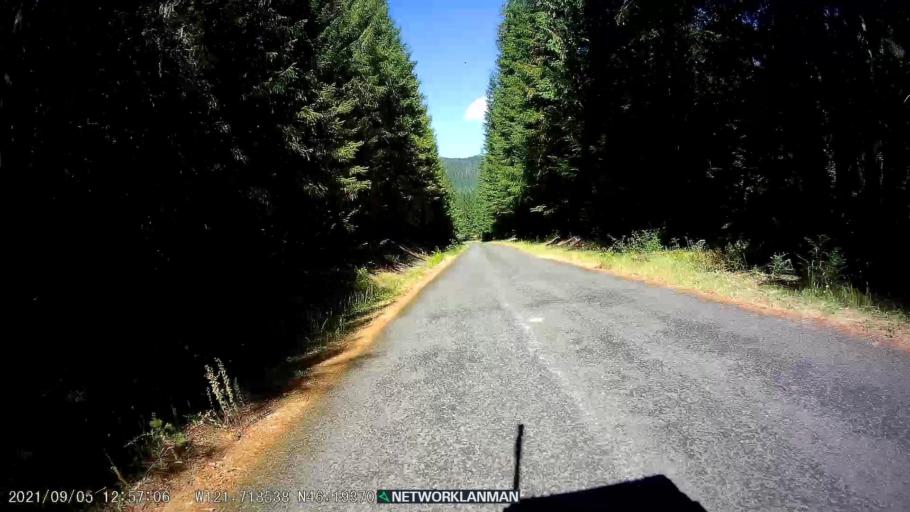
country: US
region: Washington
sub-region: Skamania County
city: Carson
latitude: 46.1934
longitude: -121.7180
